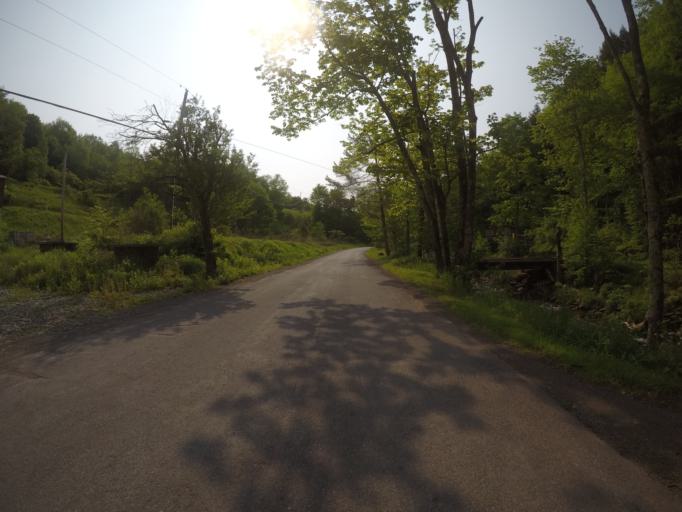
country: US
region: New York
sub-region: Sullivan County
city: Livingston Manor
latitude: 42.0823
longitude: -74.7826
